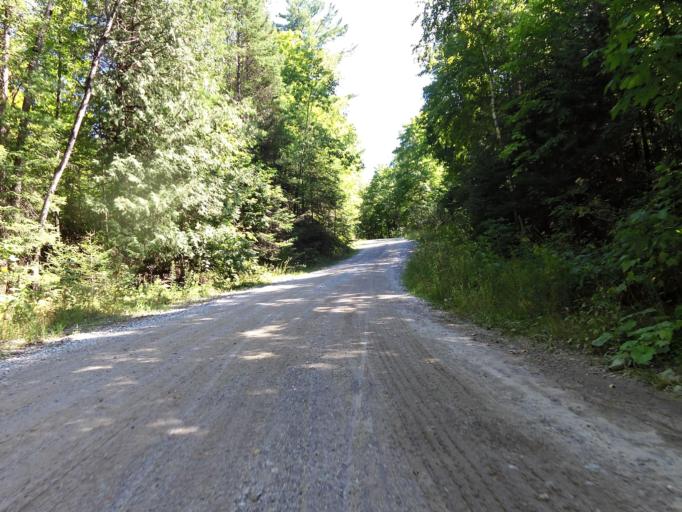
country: CA
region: Ontario
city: Renfrew
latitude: 45.1326
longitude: -76.6974
